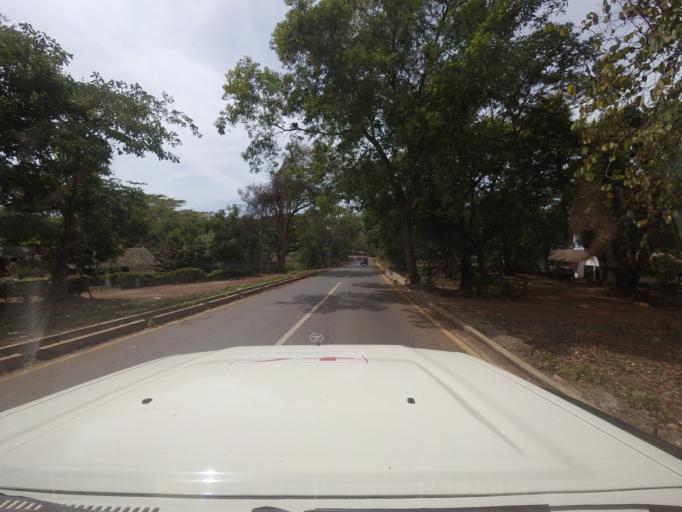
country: SL
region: Western Area
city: Freetown
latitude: 8.4715
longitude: -13.2155
